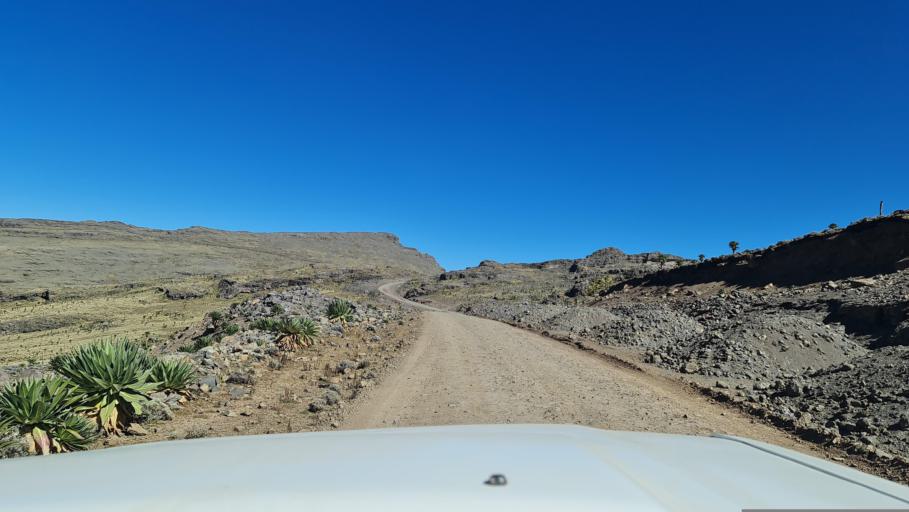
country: ET
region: Amhara
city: Debark'
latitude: 13.2168
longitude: 38.2201
